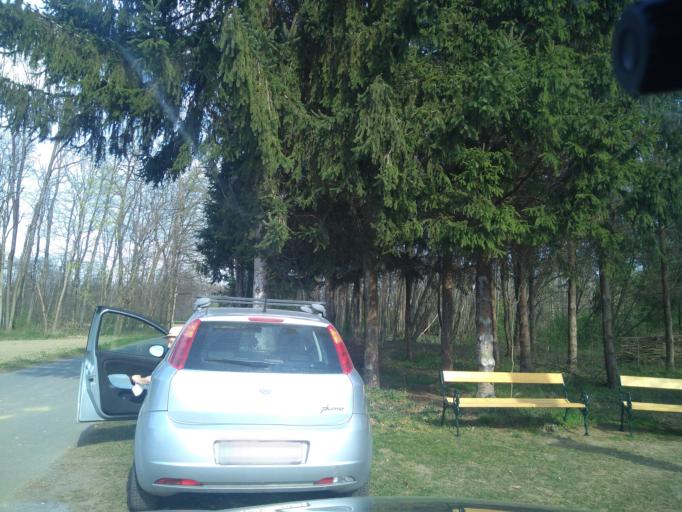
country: SI
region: Sentilj
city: Selnica ob Muri
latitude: 46.7007
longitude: 15.7312
